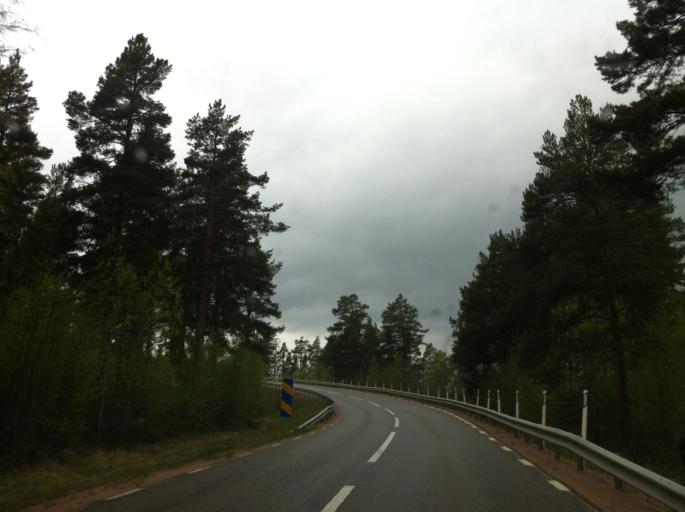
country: SE
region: Jaemtland
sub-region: Harjedalens Kommun
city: Sveg
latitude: 62.0293
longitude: 14.4156
